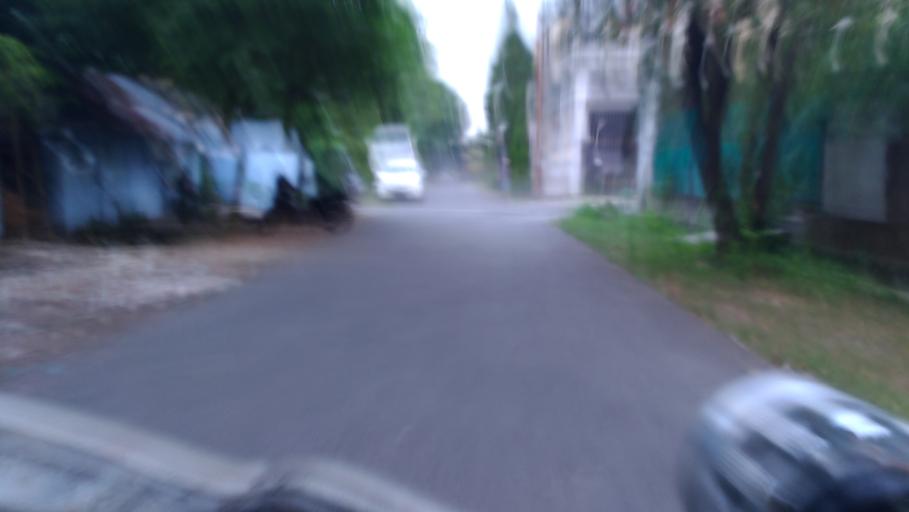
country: ID
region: West Java
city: Depok
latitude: -6.3576
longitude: 106.8665
